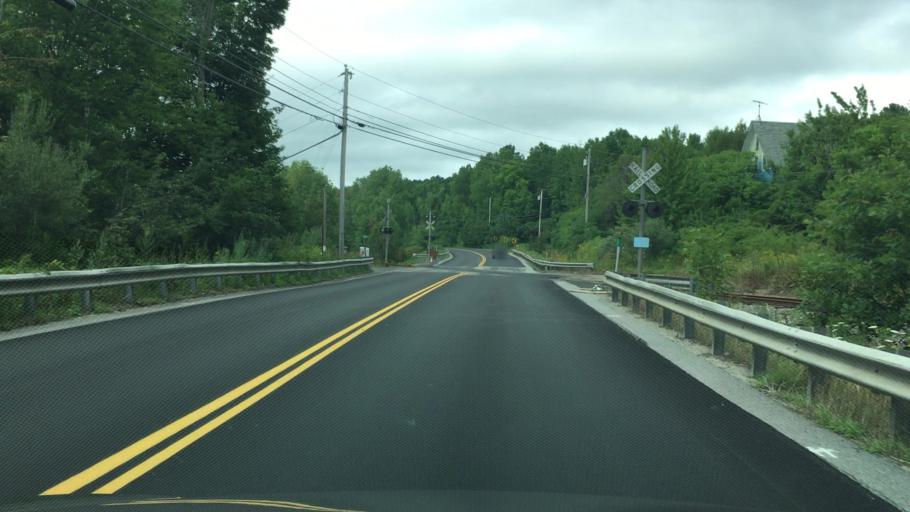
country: US
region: Maine
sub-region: Waldo County
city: Winterport
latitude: 44.6161
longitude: -68.8265
